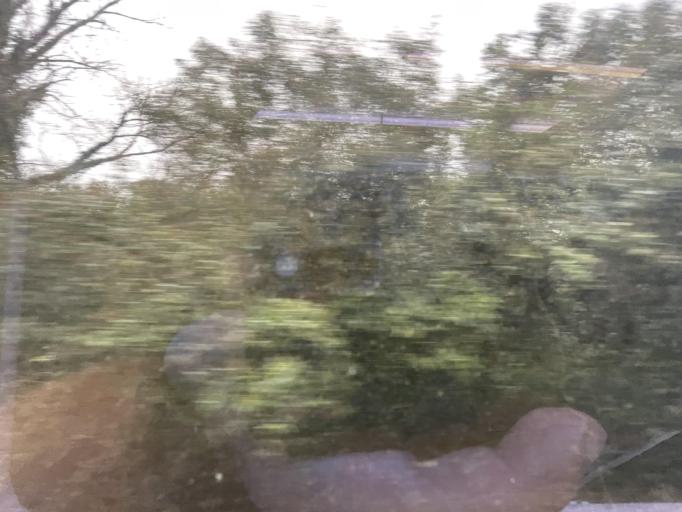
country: GE
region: Imereti
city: Vani
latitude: 42.1885
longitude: 42.4684
